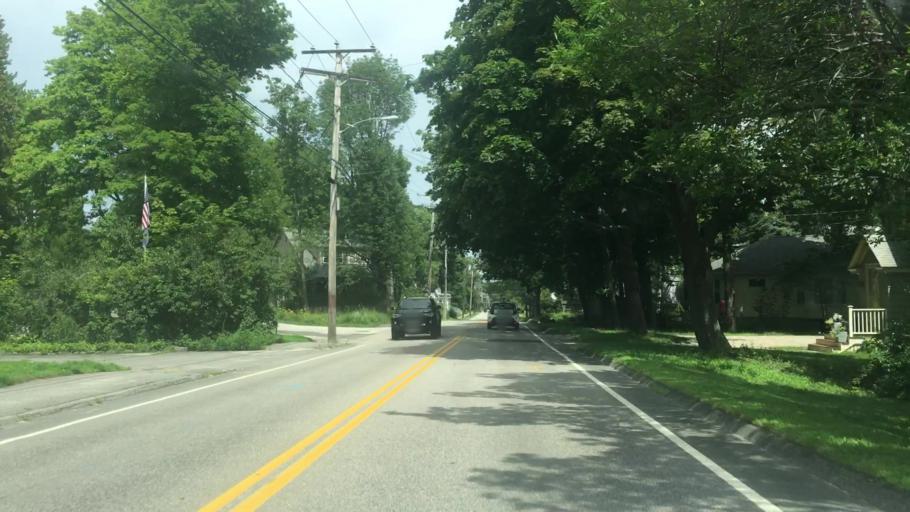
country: US
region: Maine
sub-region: Cumberland County
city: South Portland
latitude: 43.6286
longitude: -70.2560
